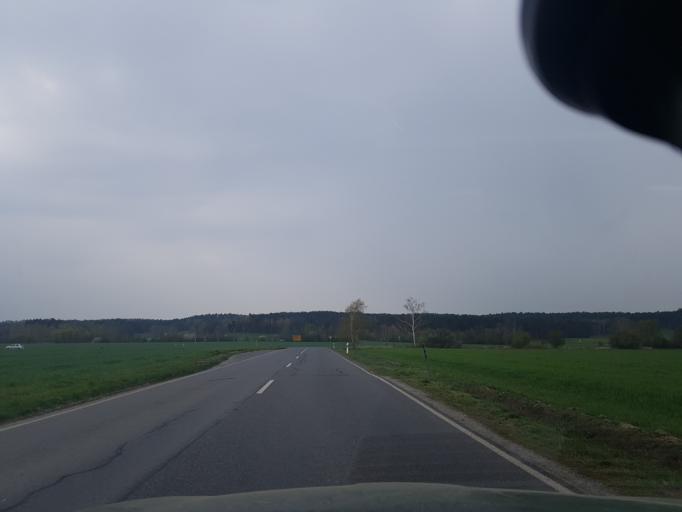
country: DE
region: Brandenburg
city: Grosskmehlen
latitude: 51.3816
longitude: 13.7113
